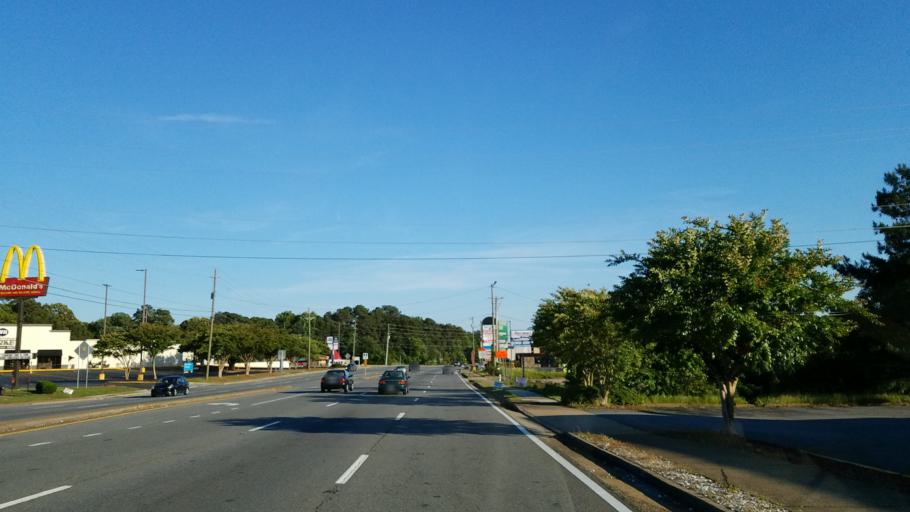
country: US
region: Georgia
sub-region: Cherokee County
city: Woodstock
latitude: 34.0866
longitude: -84.5765
